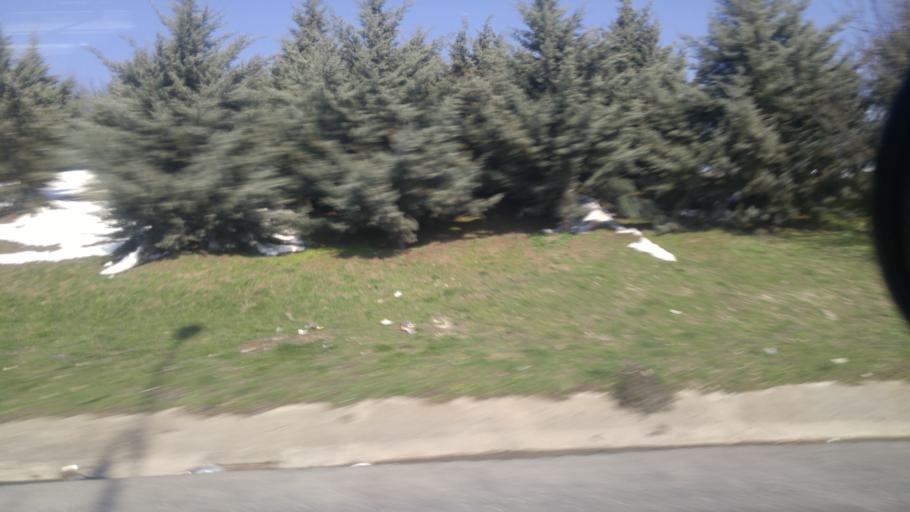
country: TR
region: Istanbul
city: Celaliye
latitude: 41.0531
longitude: 28.4310
